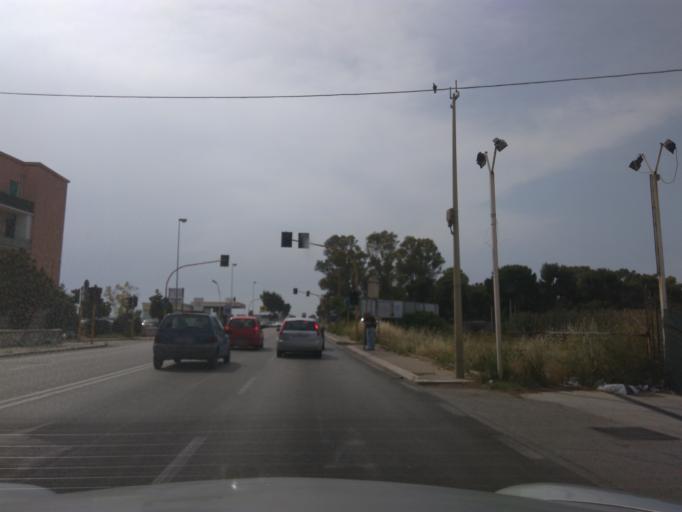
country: IT
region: Apulia
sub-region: Provincia di Bari
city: Bari
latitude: 41.1298
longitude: 16.8327
